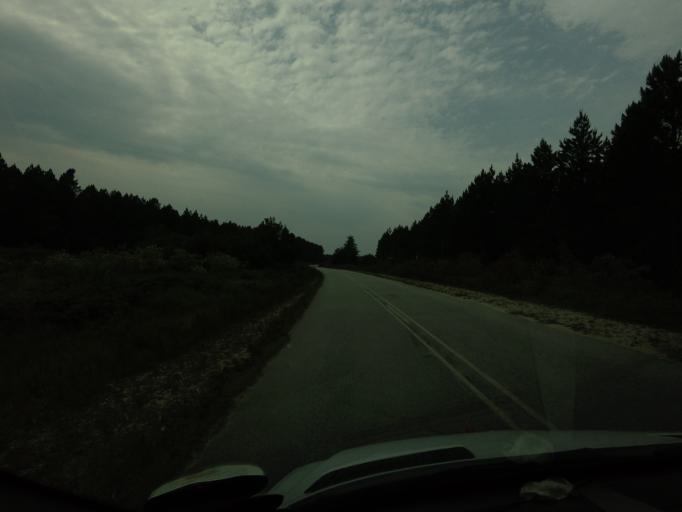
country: ZA
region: Eastern Cape
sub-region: Cacadu District Municipality
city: Kareedouw
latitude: -33.9816
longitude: 23.8410
